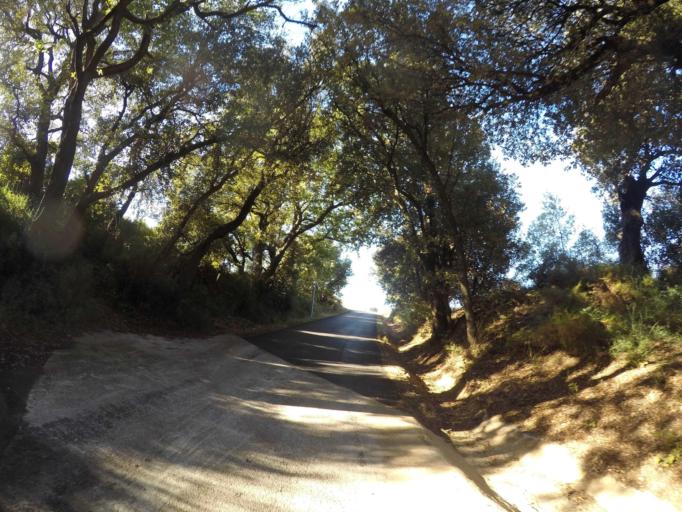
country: FR
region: Languedoc-Roussillon
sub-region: Departement des Pyrenees-Orientales
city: Llupia
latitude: 42.6017
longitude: 2.7675
